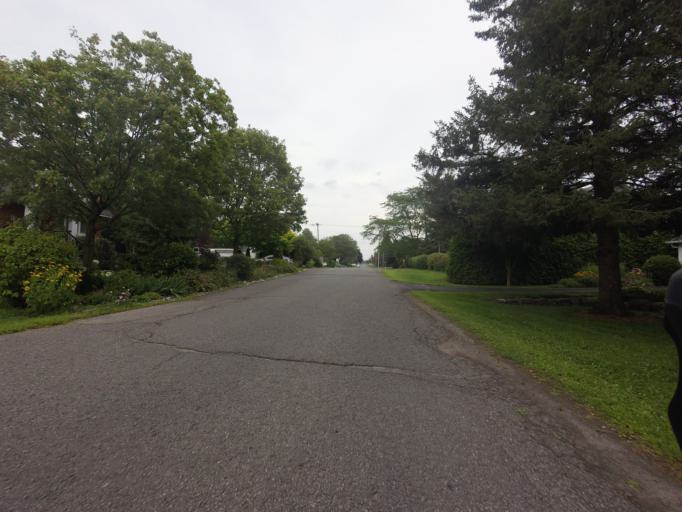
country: CA
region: Ontario
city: Ottawa
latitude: 45.3514
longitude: -75.7457
